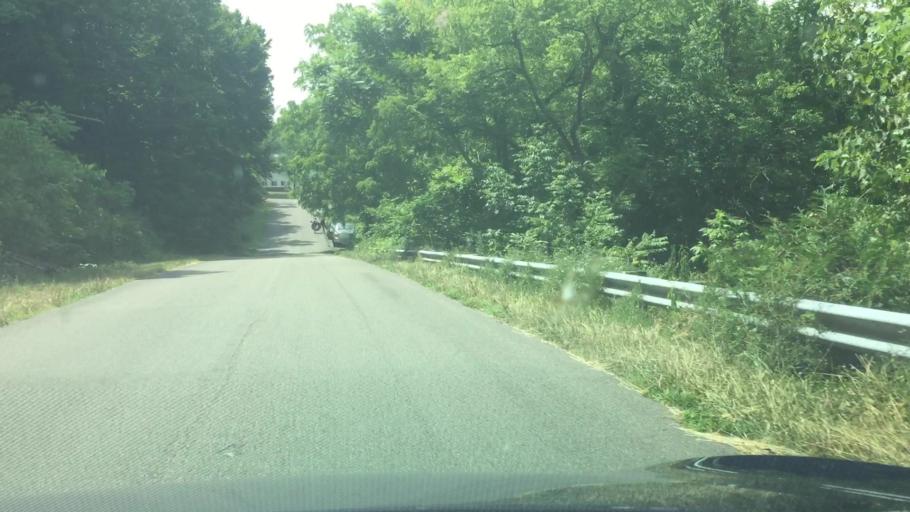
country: US
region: Virginia
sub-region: Wythe County
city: Wytheville
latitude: 36.9334
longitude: -81.0716
